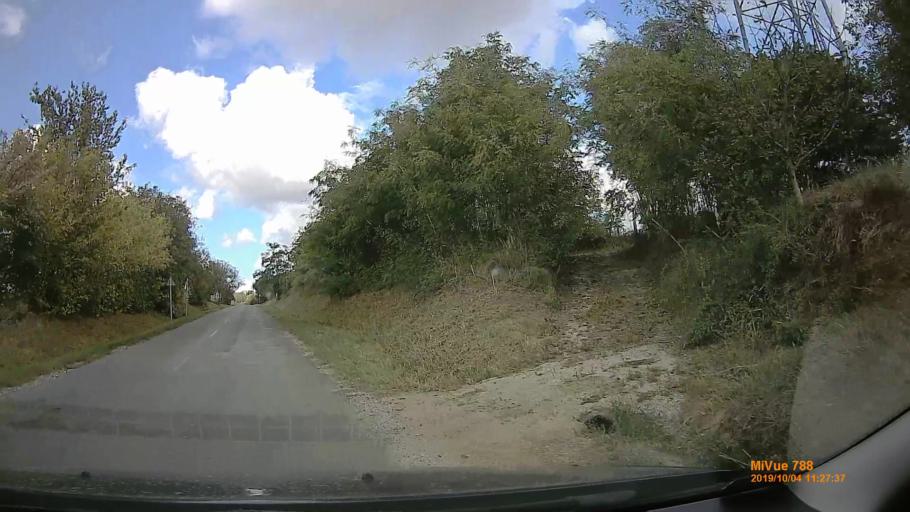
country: HU
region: Somogy
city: Kaposvar
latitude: 46.5164
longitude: 17.8078
